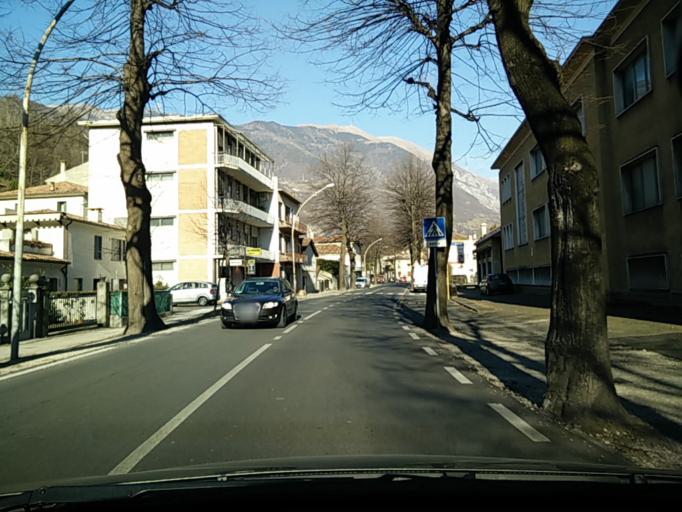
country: IT
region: Veneto
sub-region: Provincia di Treviso
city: Revine
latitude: 46.0041
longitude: 12.2861
